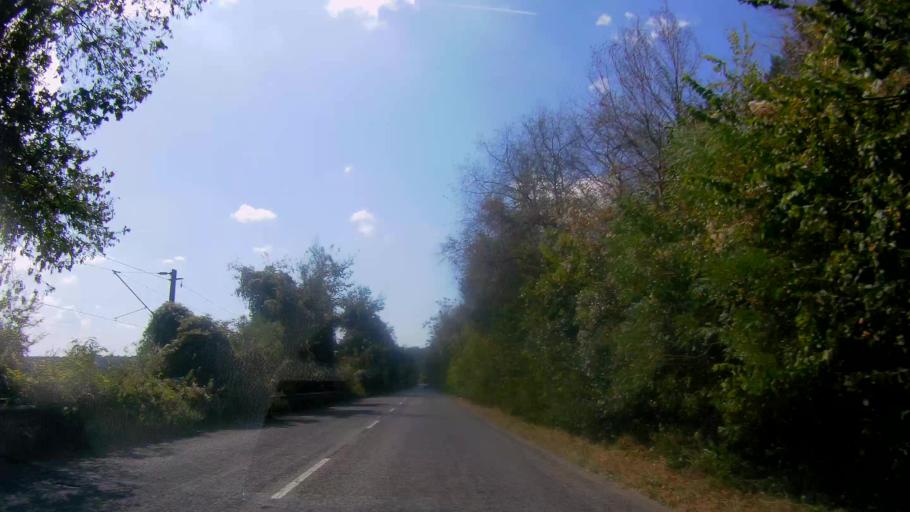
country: BG
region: Veliko Turnovo
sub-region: Obshtina Polski Trumbesh
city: Polski Trumbesh
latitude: 43.4439
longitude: 25.6562
